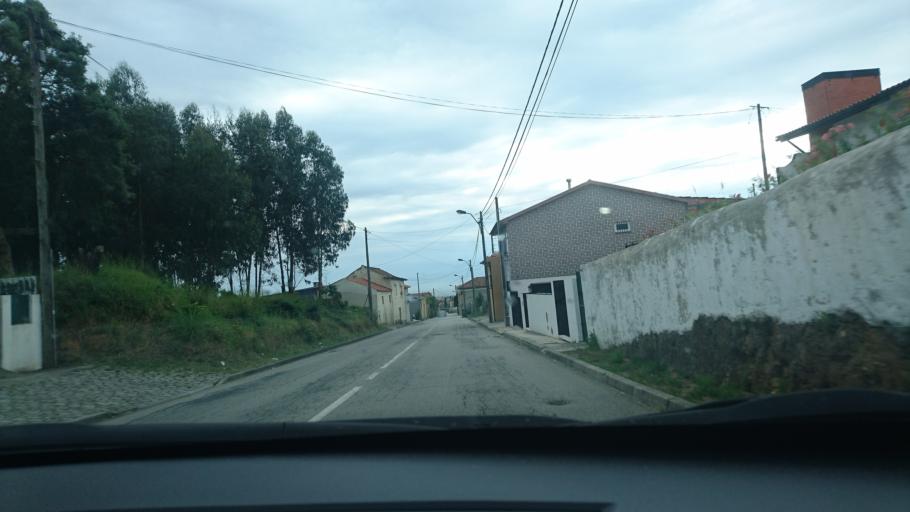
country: PT
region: Aveiro
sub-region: Ovar
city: Cortegaca
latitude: 40.9613
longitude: -8.6123
